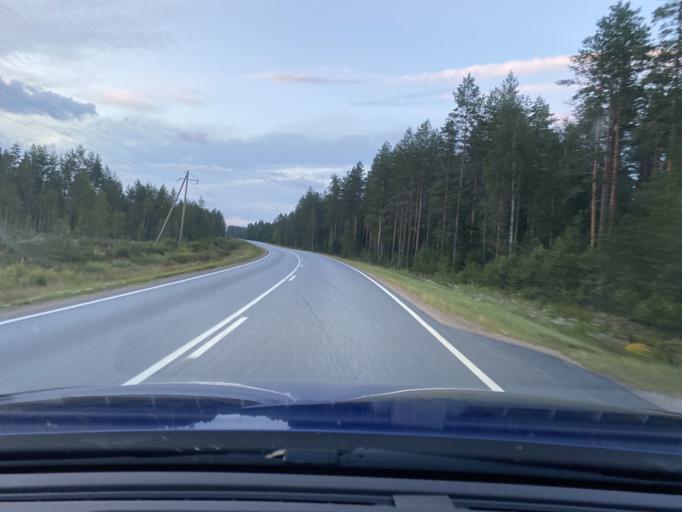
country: FI
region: Satakunta
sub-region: Pohjois-Satakunta
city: Honkajoki
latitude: 62.1783
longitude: 22.2886
